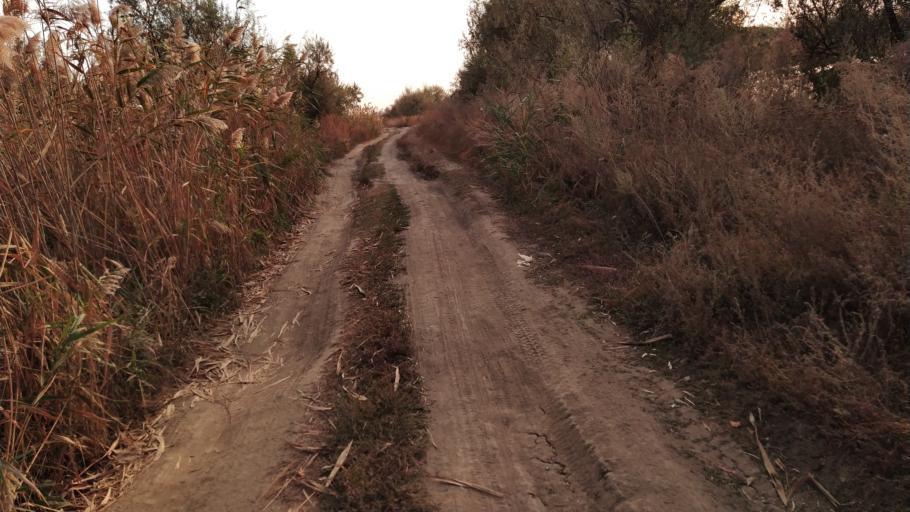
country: RU
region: Rostov
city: Kuleshovka
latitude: 47.1212
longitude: 39.6037
